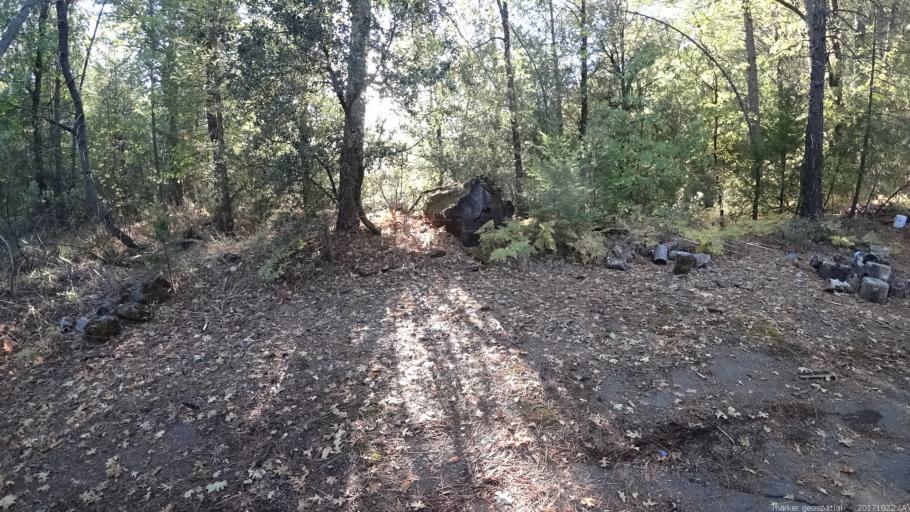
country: US
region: California
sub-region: Shasta County
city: Shasta Lake
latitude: 40.8539
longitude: -122.3305
